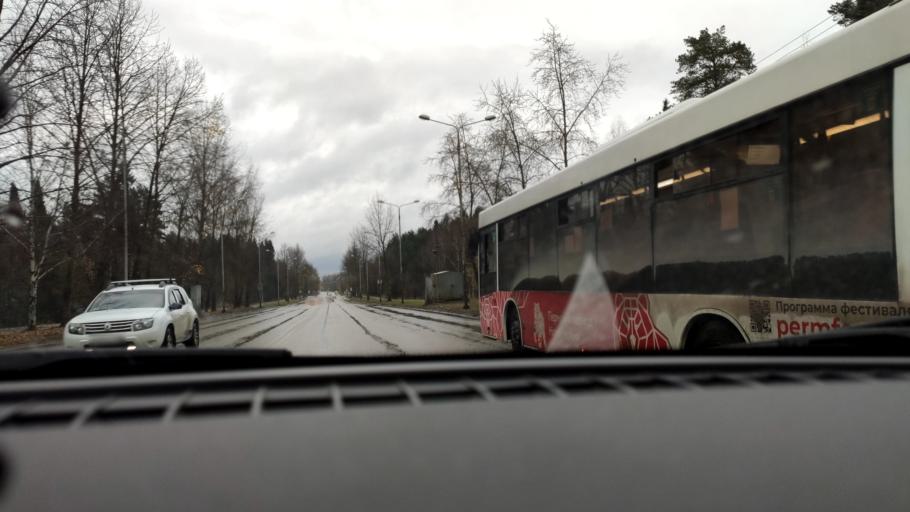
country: RU
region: Perm
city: Perm
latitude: 58.0835
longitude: 56.3762
